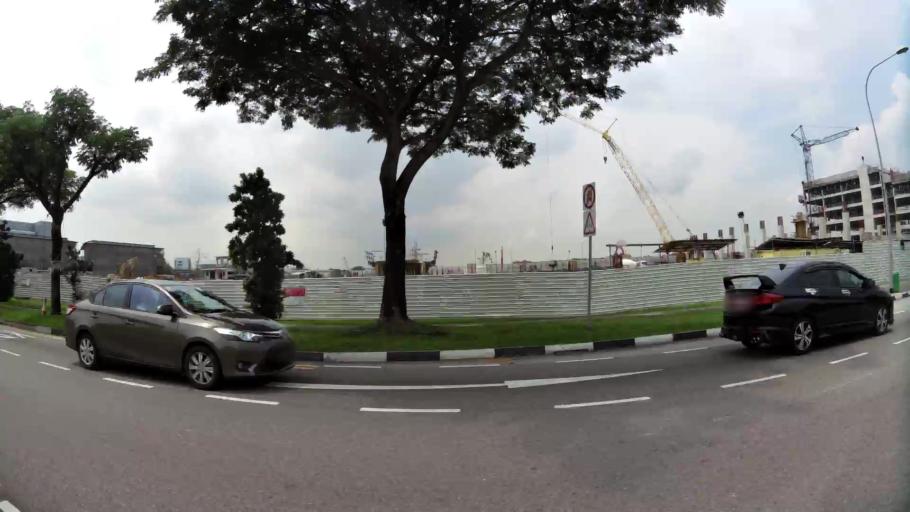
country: SG
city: Singapore
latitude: 1.3430
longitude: 103.8990
